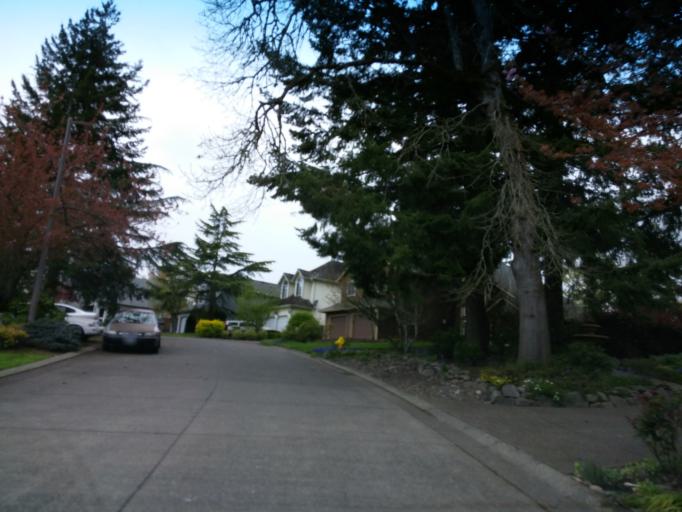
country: US
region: Oregon
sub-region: Washington County
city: Oak Hills
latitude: 45.5290
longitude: -122.8529
